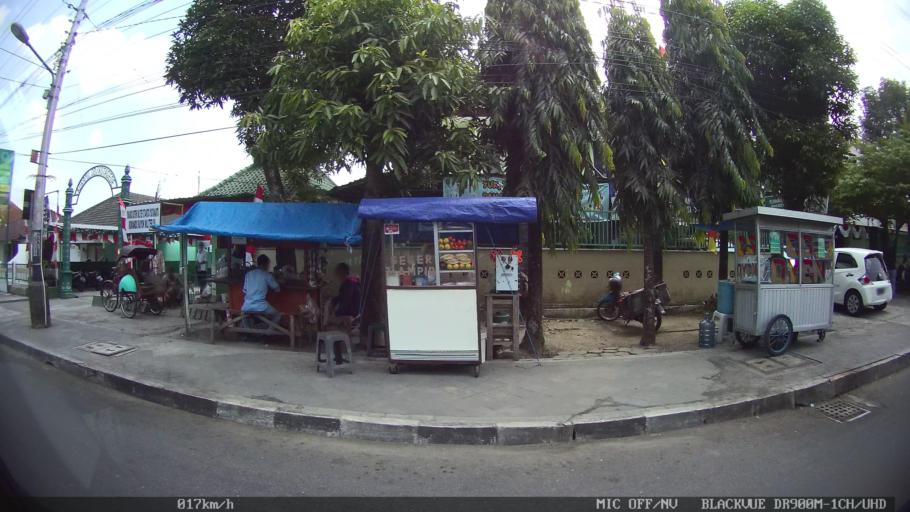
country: ID
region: Daerah Istimewa Yogyakarta
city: Yogyakarta
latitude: -7.8223
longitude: 110.4006
